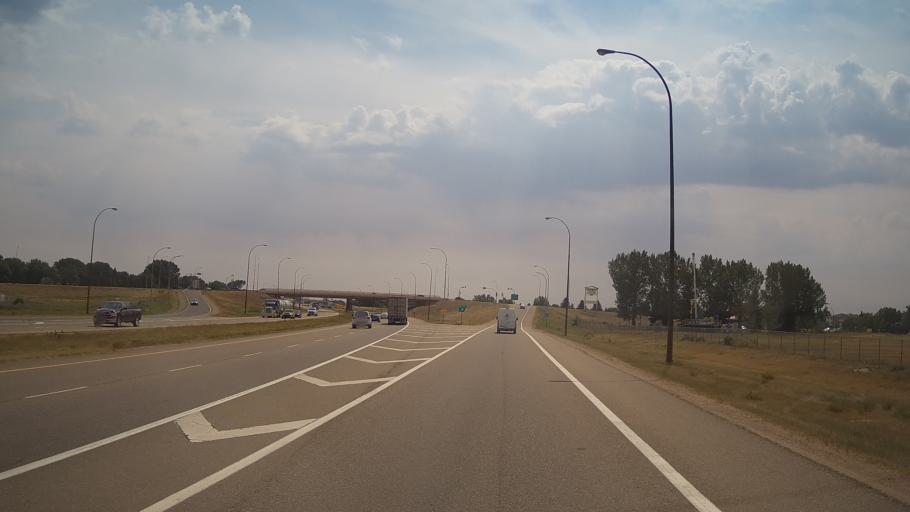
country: CA
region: Alberta
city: Medicine Hat
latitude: 50.0139
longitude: -110.6866
